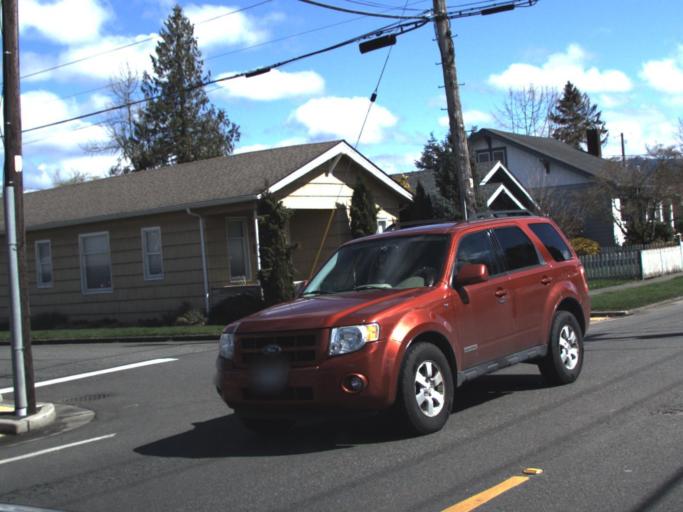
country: US
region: Washington
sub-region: King County
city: Enumclaw
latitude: 47.2066
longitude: -121.9974
